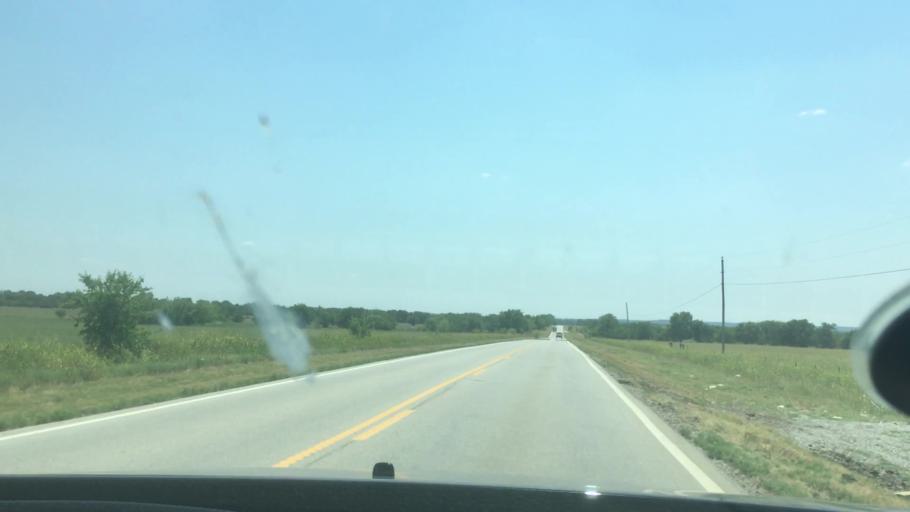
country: US
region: Oklahoma
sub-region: Bryan County
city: Durant
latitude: 34.1388
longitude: -96.3732
